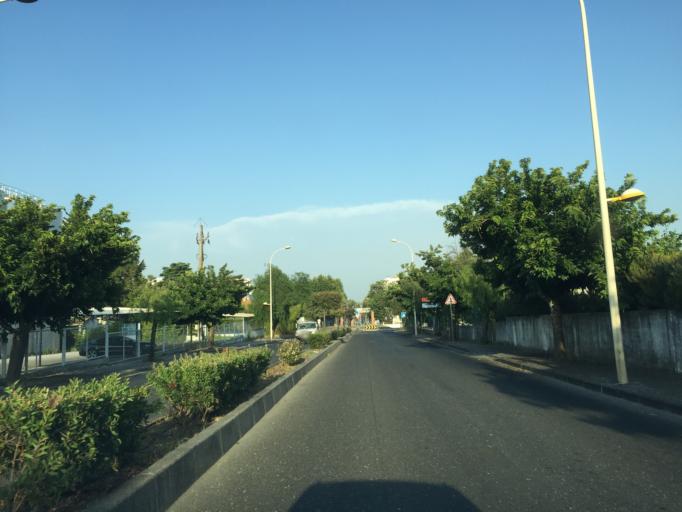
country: PT
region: Santarem
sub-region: Torres Novas
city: Torres Novas
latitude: 39.4728
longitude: -8.5489
